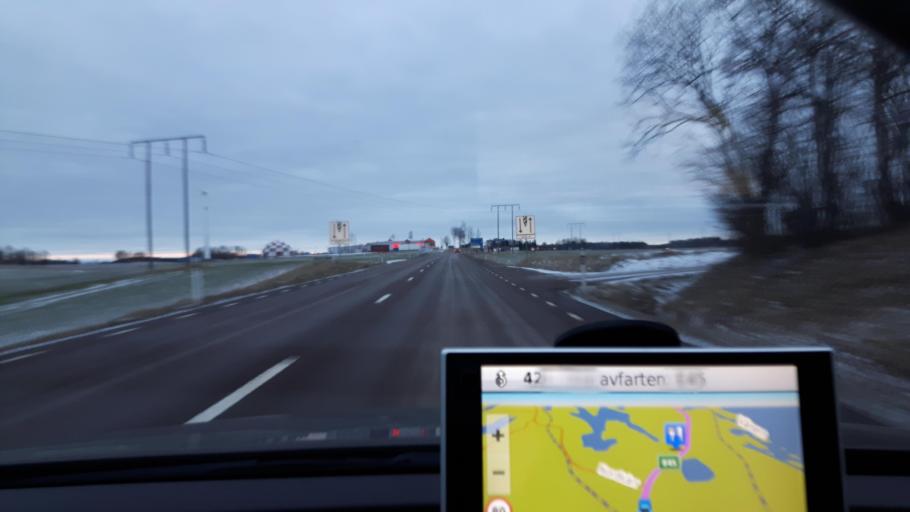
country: SE
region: Vaestra Goetaland
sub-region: Melleruds Kommun
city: Mellerud
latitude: 58.7269
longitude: 12.4533
